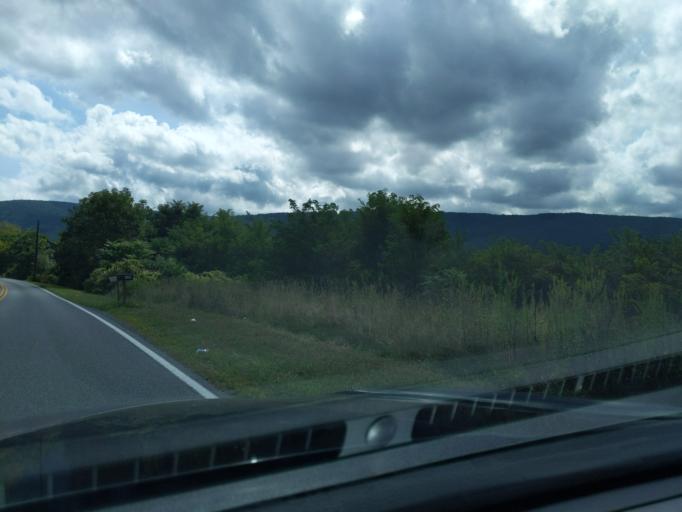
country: US
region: Pennsylvania
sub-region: Blair County
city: Duncansville
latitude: 40.3953
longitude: -78.4259
